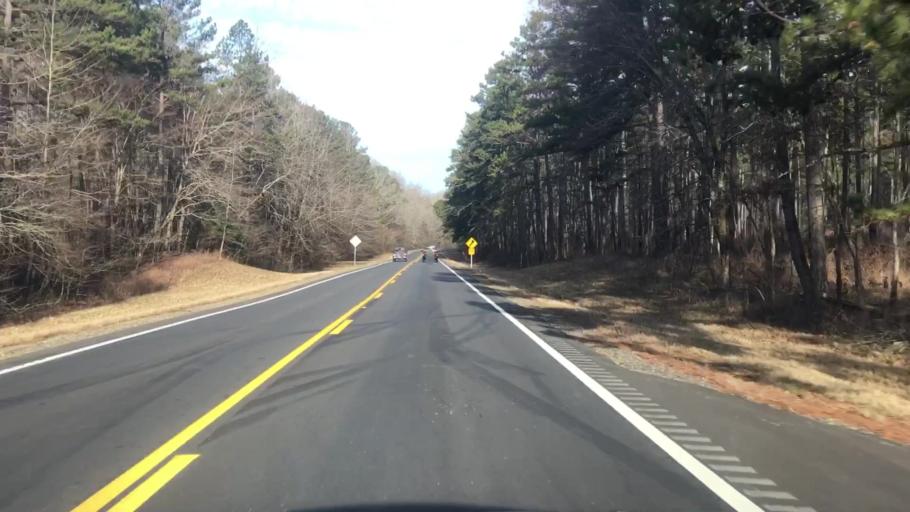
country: US
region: Arkansas
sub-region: Montgomery County
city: Mount Ida
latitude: 34.5175
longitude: -93.3858
